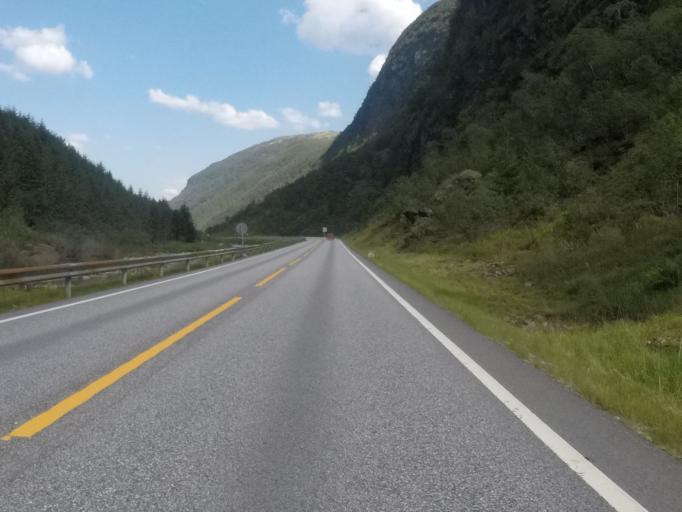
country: NO
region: Hordaland
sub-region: Masfjorden
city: Masfjorden
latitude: 60.9694
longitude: 5.4866
